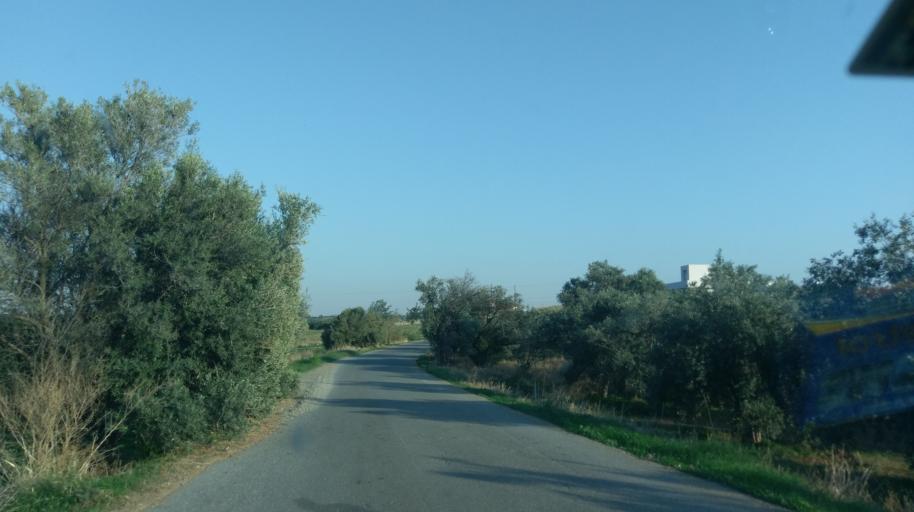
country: CY
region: Lefkosia
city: Lefka
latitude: 35.1355
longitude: 32.9164
